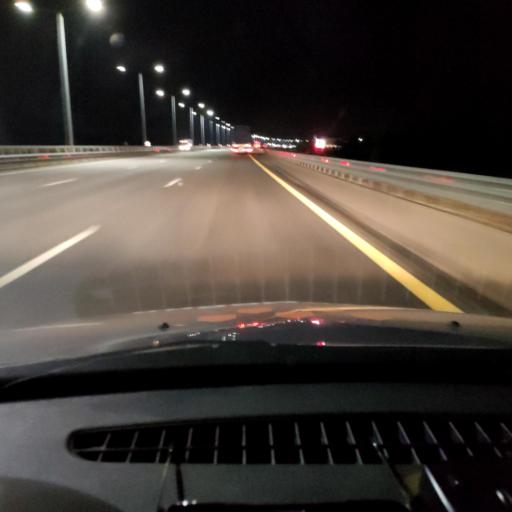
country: RU
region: Voronezj
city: Somovo
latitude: 51.7838
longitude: 39.2904
